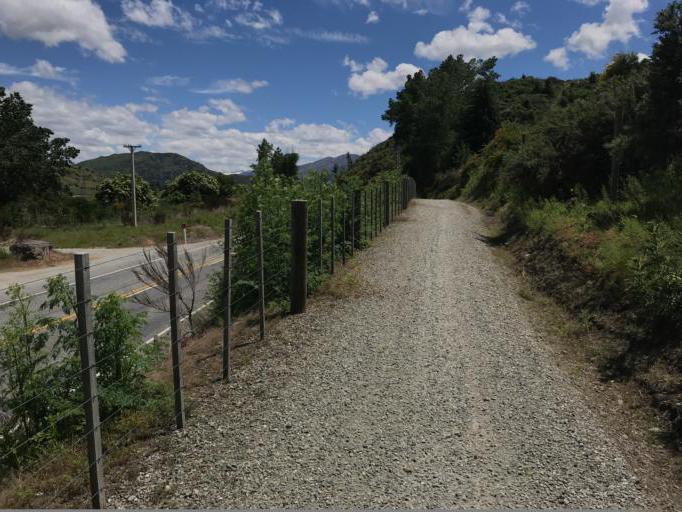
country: NZ
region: Otago
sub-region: Queenstown-Lakes District
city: Arrowtown
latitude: -45.0081
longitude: 168.8852
